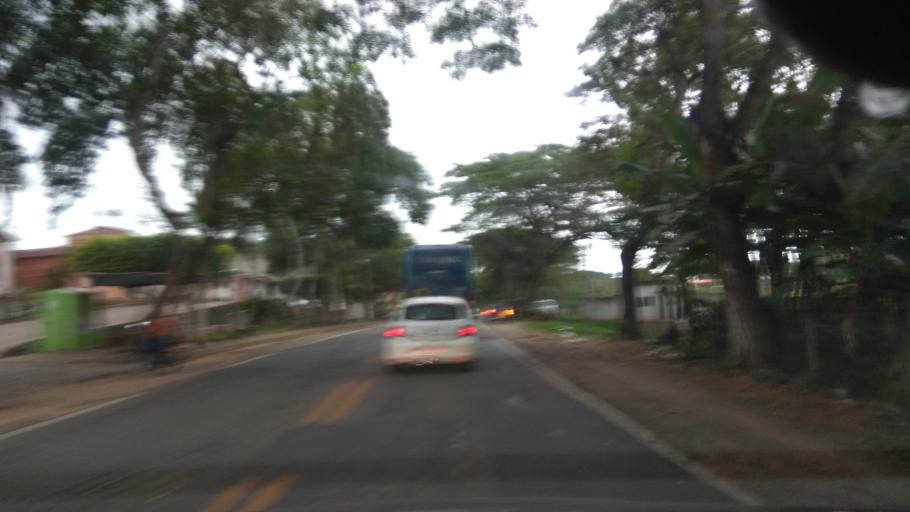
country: BR
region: Bahia
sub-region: Ubata
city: Ubata
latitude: -14.1991
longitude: -39.5367
